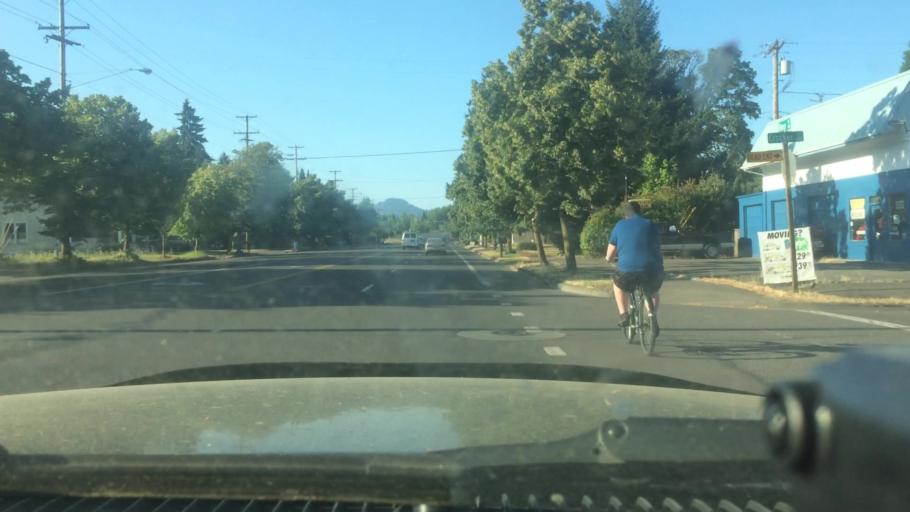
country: US
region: Oregon
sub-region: Lane County
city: Eugene
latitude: 44.0678
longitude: -123.1180
